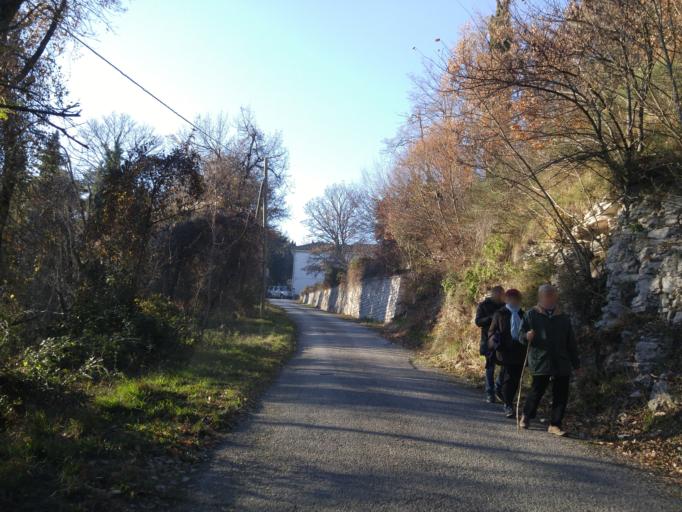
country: IT
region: The Marches
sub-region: Provincia di Pesaro e Urbino
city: Fossombrone
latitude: 43.6925
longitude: 12.7808
